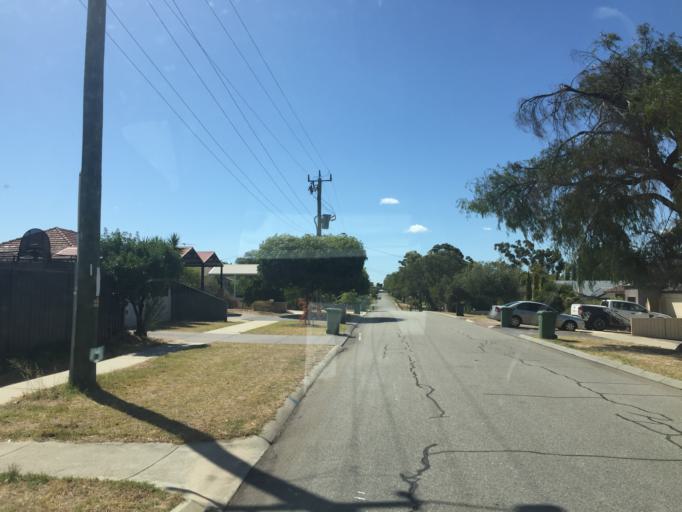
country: AU
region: Western Australia
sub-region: Belmont
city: Redcliffe
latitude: -31.9375
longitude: 115.9426
